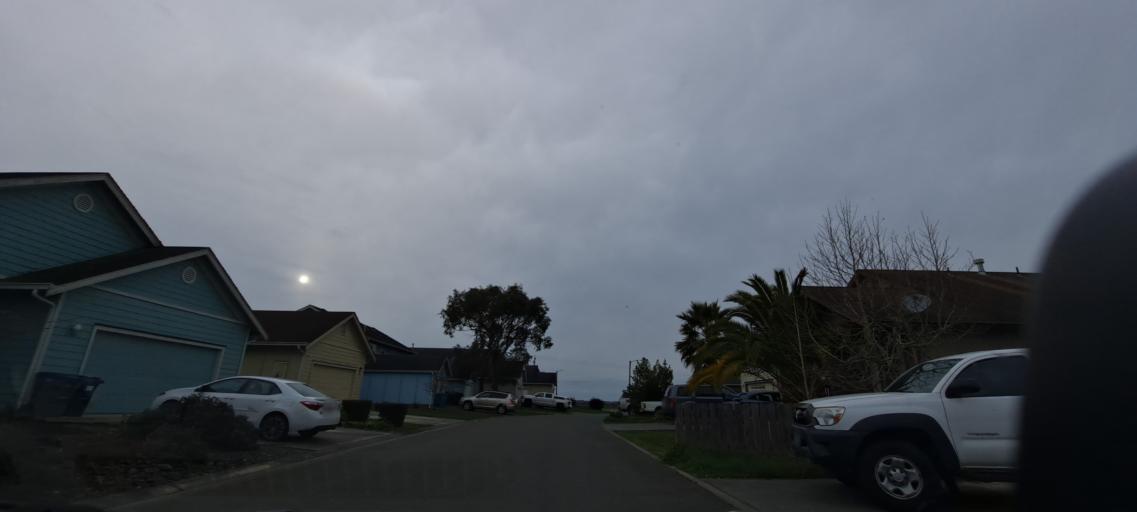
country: US
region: California
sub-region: Humboldt County
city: Arcata
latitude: 40.8713
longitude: -124.1046
